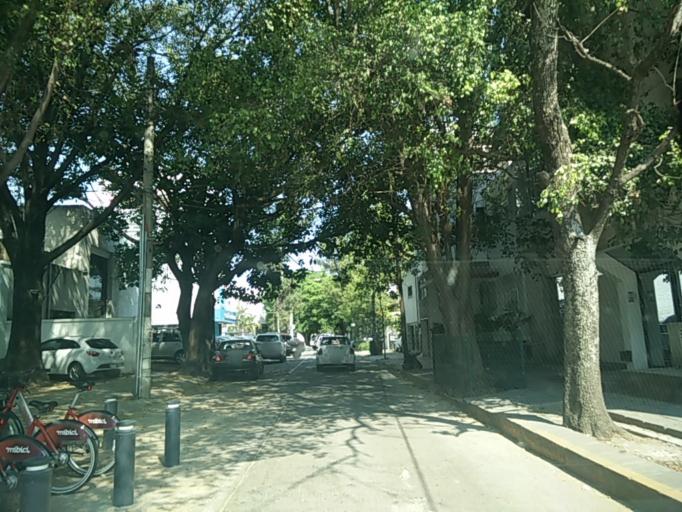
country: MX
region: Jalisco
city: Guadalajara
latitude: 20.6737
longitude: -103.3725
